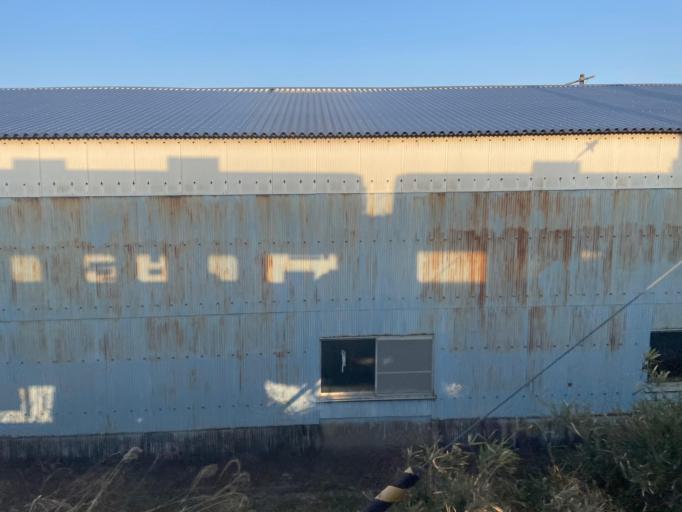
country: JP
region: Gunma
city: Kanekomachi
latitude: 36.4198
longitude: 139.0315
